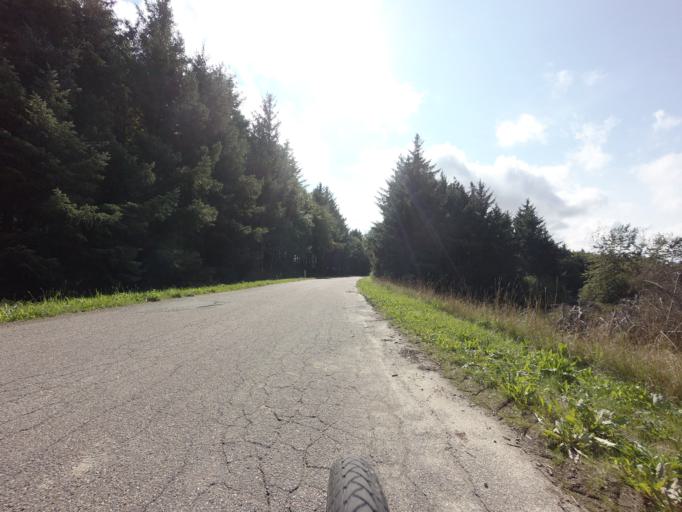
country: DK
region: North Denmark
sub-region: Hjorring Kommune
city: Hjorring
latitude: 57.5387
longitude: 10.0583
